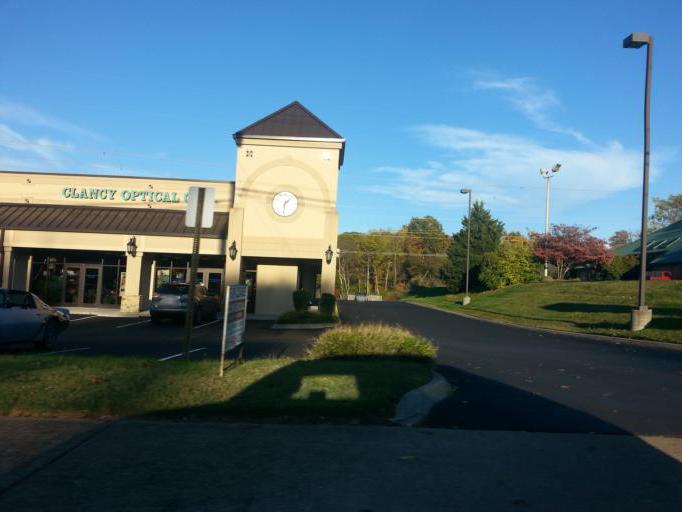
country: US
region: Tennessee
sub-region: Knox County
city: Farragut
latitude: 35.9117
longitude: -84.0811
